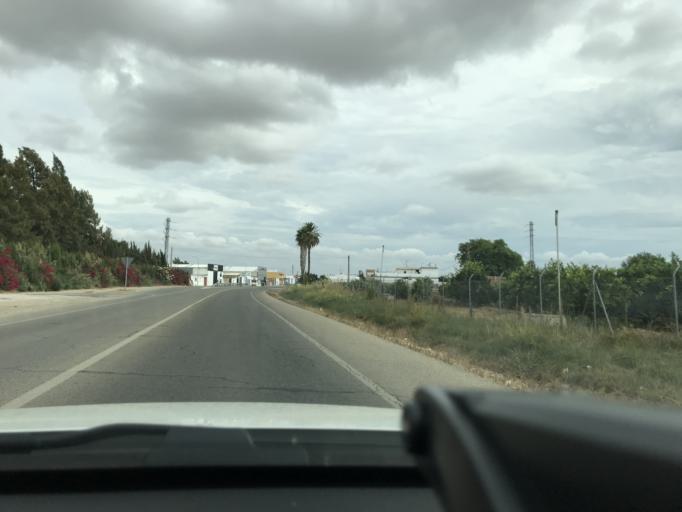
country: ES
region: Andalusia
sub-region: Provincia de Sevilla
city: La Rinconada
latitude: 37.4742
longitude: -5.9749
